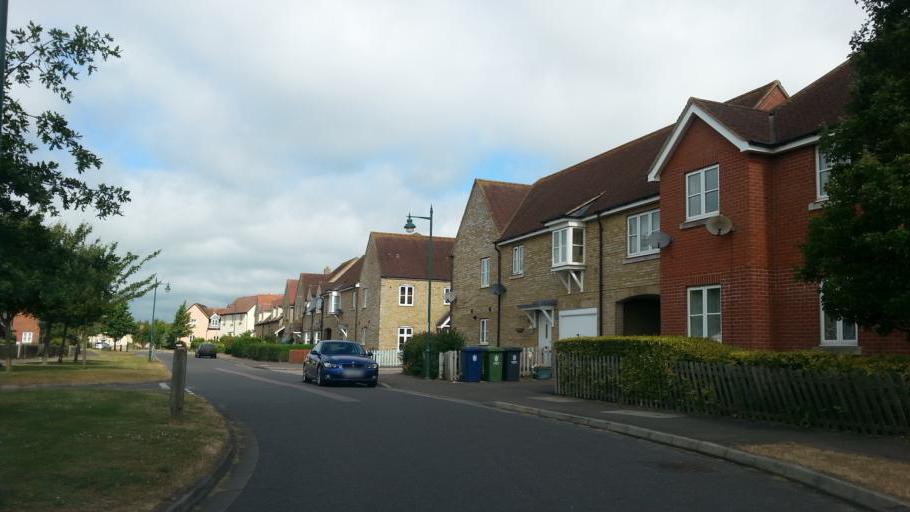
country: GB
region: England
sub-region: Cambridgeshire
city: Papworth Everard
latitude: 52.2176
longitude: -0.0825
